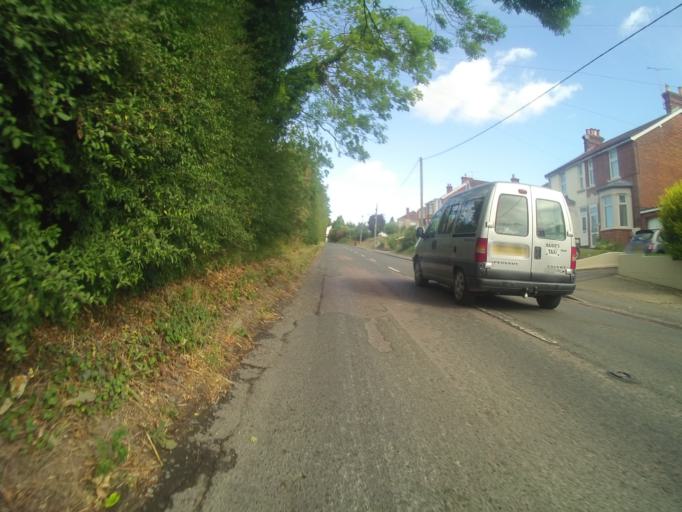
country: GB
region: England
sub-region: Wiltshire
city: Durrington
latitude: 51.1932
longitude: -1.7681
